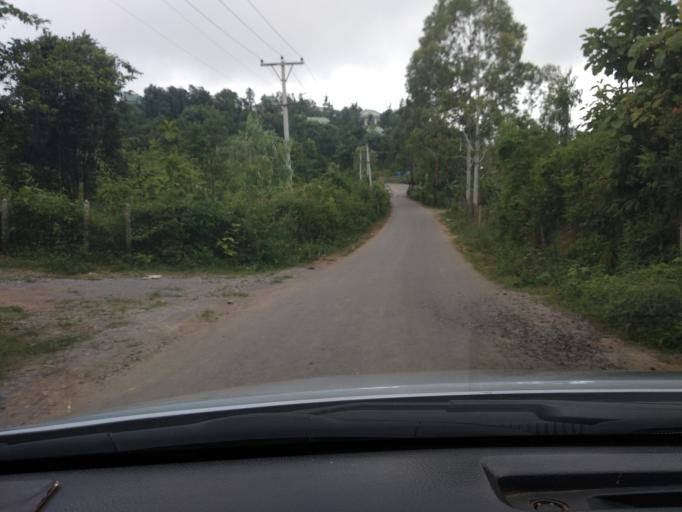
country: MM
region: Mandalay
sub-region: Pyin Oo Lwin District
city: Pyin Oo Lwin
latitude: 21.9151
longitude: 96.3834
